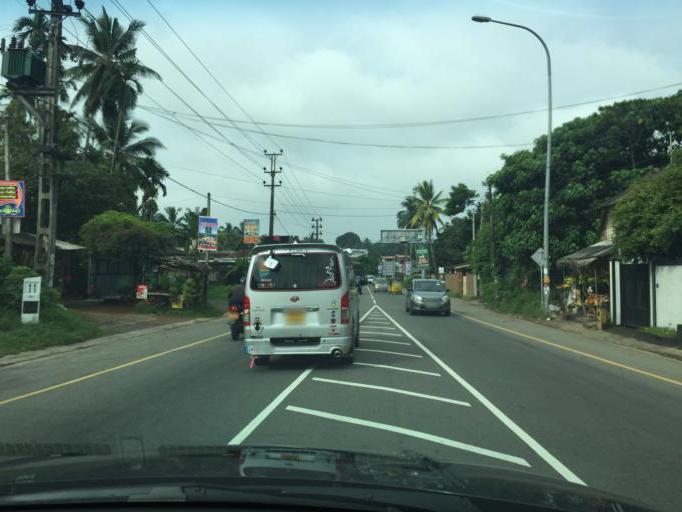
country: LK
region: Western
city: Horana South
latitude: 6.7187
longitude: 79.9979
